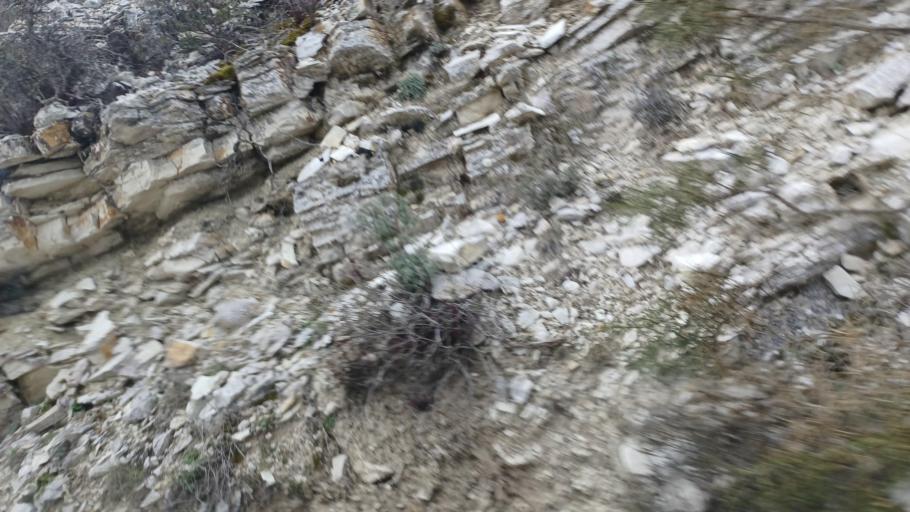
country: CY
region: Limassol
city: Pachna
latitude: 34.8678
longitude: 32.8039
